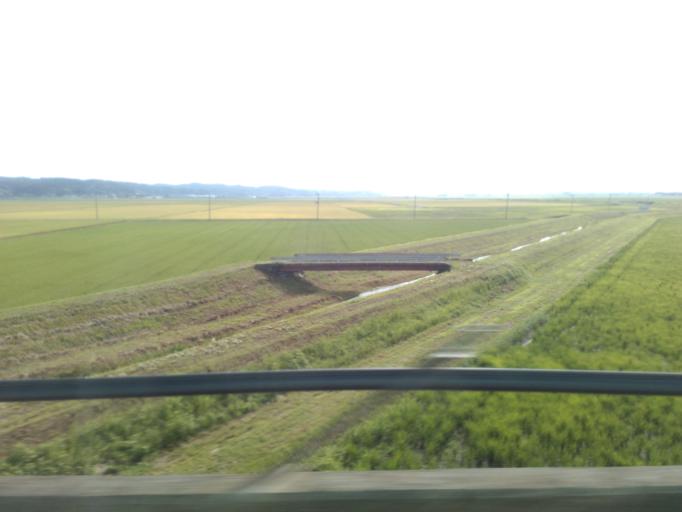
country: JP
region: Iwate
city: Ichinoseki
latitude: 38.7998
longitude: 141.0961
